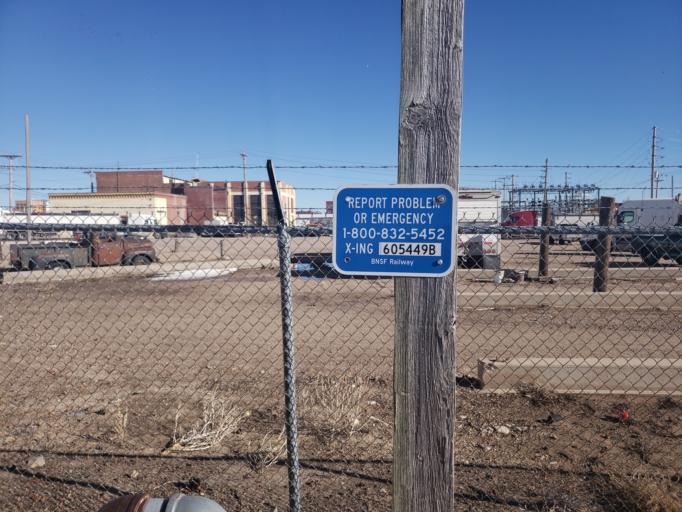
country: US
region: Kansas
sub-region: Ford County
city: Dodge City
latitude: 37.7513
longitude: -100.0258
